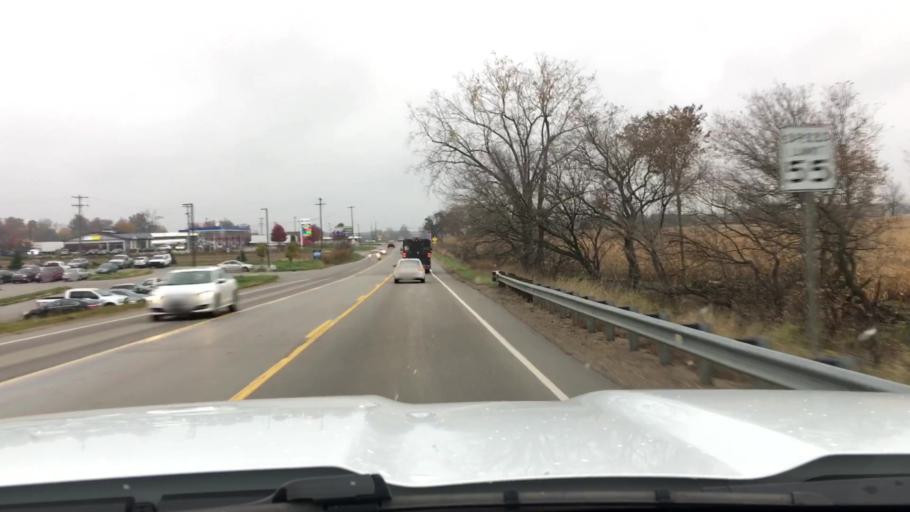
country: US
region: Michigan
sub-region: Kent County
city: Lowell
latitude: 42.8816
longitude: -85.3709
